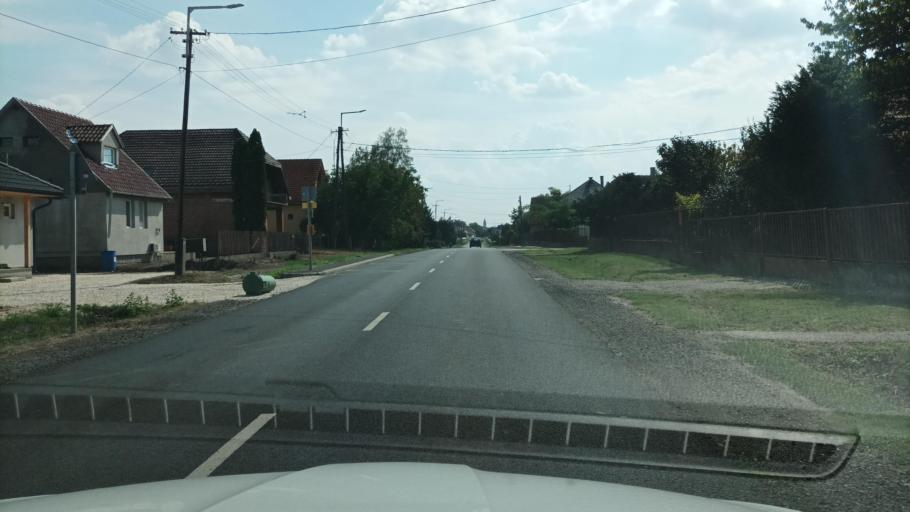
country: HU
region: Pest
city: Zsambok
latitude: 47.5553
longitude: 19.6047
